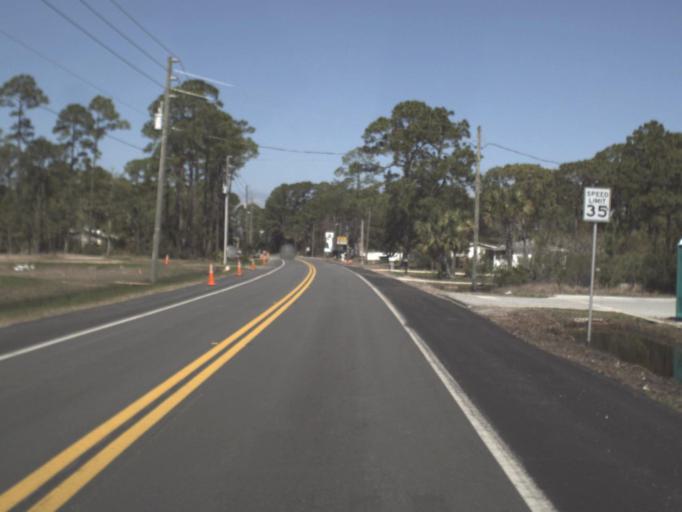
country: US
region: Florida
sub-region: Gulf County
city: Port Saint Joe
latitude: 29.7407
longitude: -85.3012
